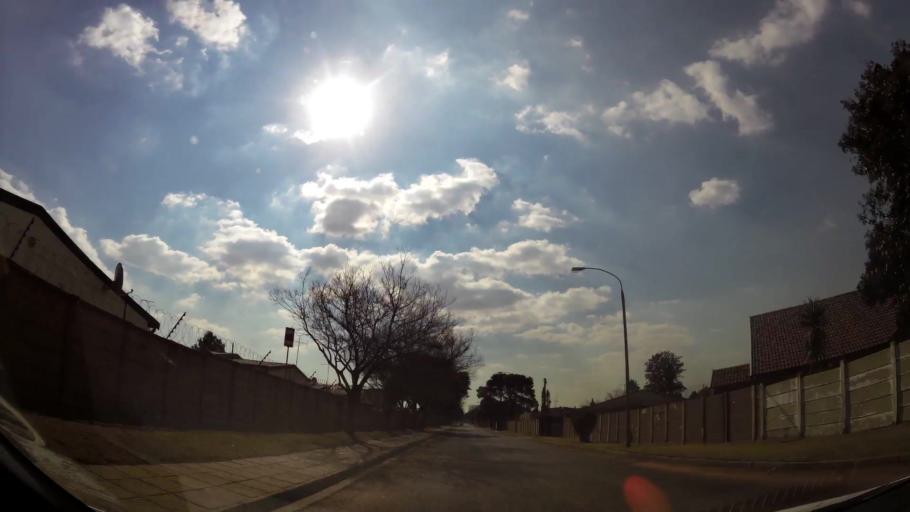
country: ZA
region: Gauteng
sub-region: Ekurhuleni Metropolitan Municipality
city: Germiston
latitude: -26.1838
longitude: 28.2021
